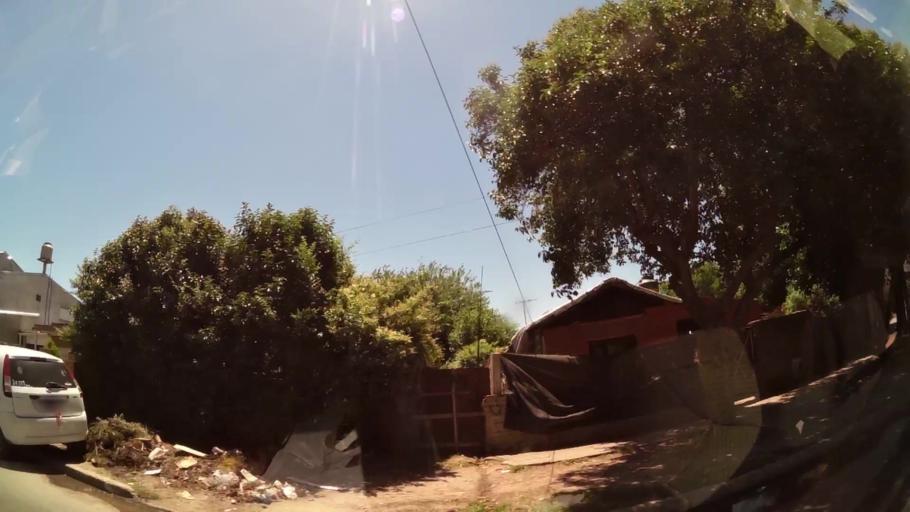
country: AR
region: Buenos Aires
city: Hurlingham
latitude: -34.5113
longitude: -58.7061
